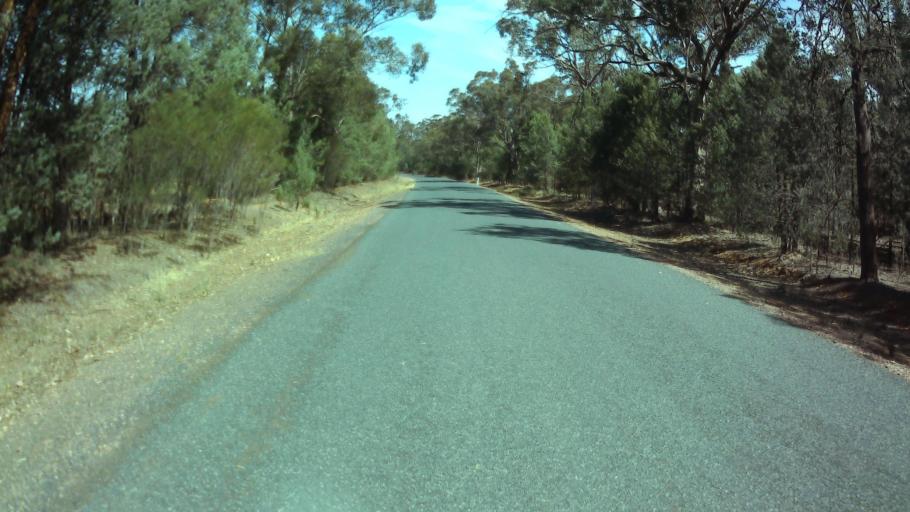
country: AU
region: New South Wales
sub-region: Weddin
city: Grenfell
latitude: -34.0695
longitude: 148.1389
